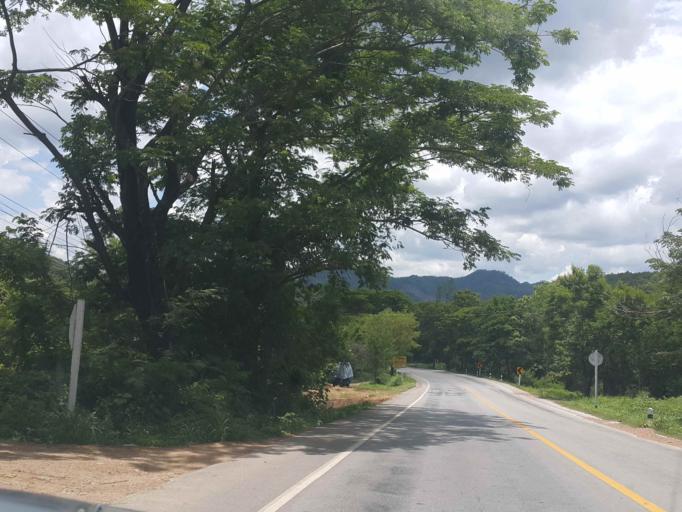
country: TH
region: Nan
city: Wiang Sa
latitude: 18.5241
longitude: 100.5688
